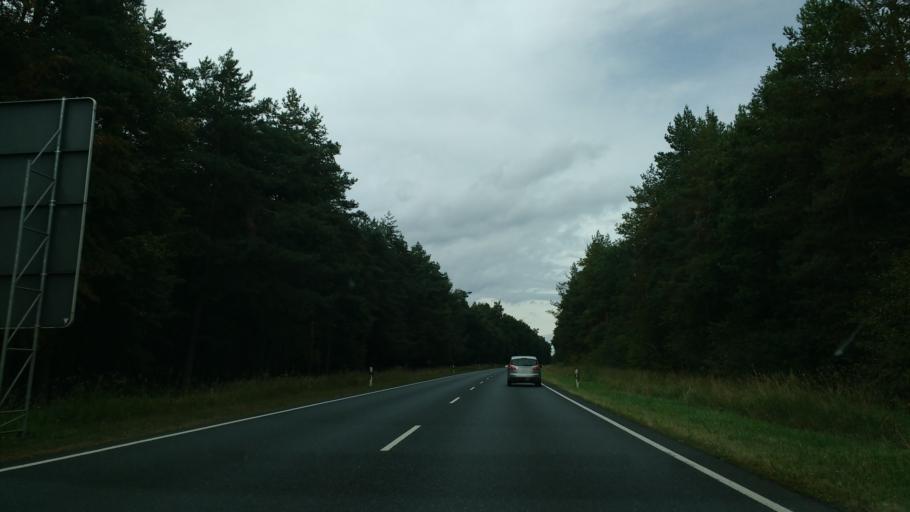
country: DE
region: Bavaria
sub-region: Regierungsbezirk Unterfranken
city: Schwebheim
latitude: 49.9973
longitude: 10.2381
